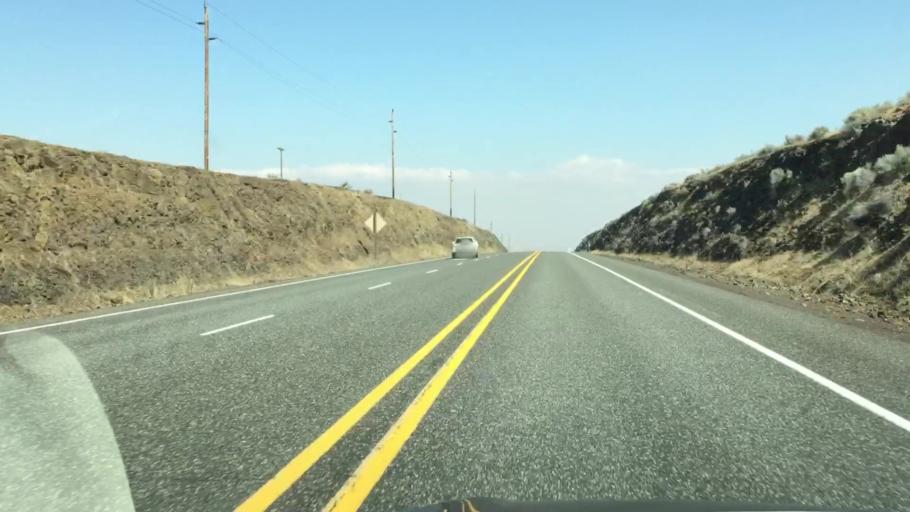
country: US
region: Oregon
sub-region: Wasco County
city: The Dalles
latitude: 45.3593
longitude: -121.1421
